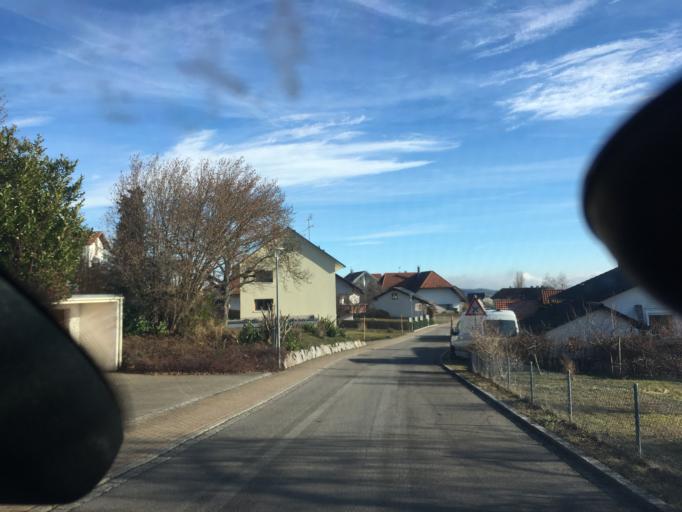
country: DE
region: Baden-Wuerttemberg
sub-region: Freiburg Region
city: Gorwihl
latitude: 47.6430
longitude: 8.0692
